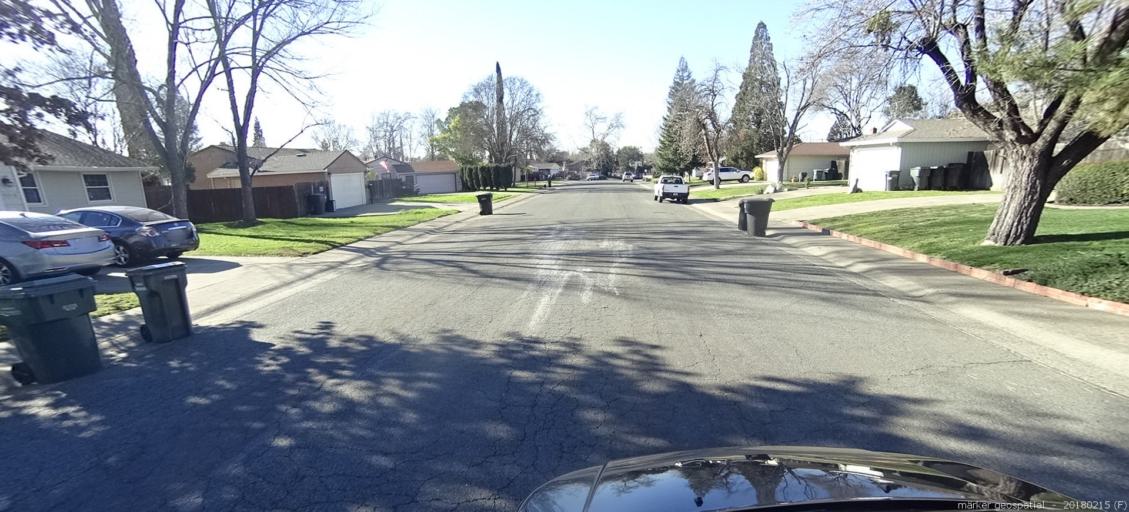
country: US
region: California
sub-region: Sacramento County
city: Foothill Farms
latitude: 38.6657
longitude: -121.3235
